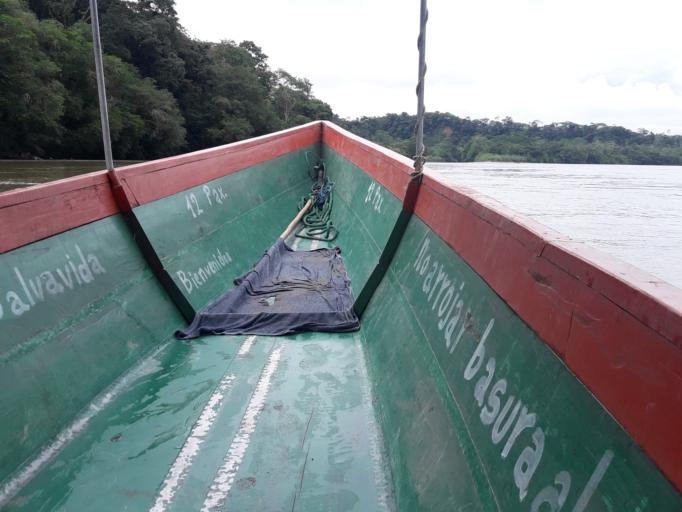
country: EC
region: Napo
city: Tena
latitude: -1.0357
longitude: -77.6629
